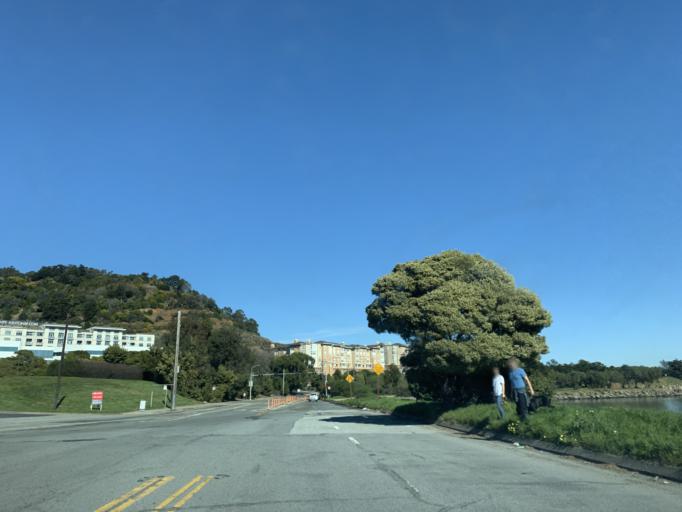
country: US
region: California
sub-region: San Mateo County
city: Brisbane
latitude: 37.7088
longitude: -122.3929
